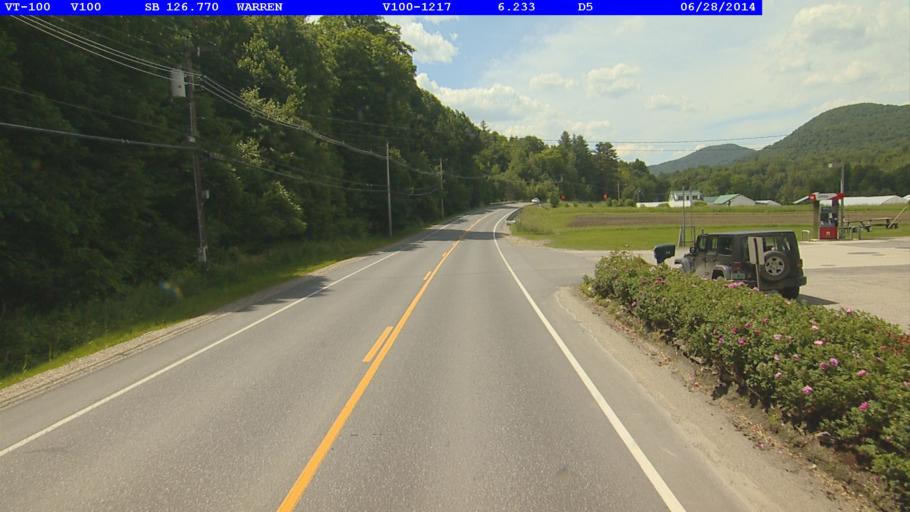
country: US
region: Vermont
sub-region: Washington County
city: Northfield
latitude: 44.1449
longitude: -72.8411
